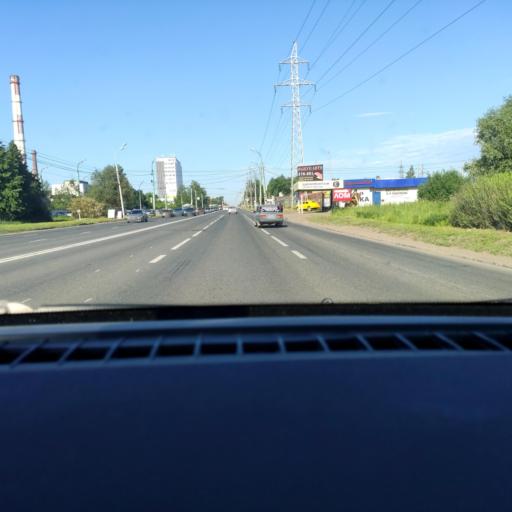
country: RU
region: Udmurtiya
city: Khokhryaki
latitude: 56.8965
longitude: 53.2922
